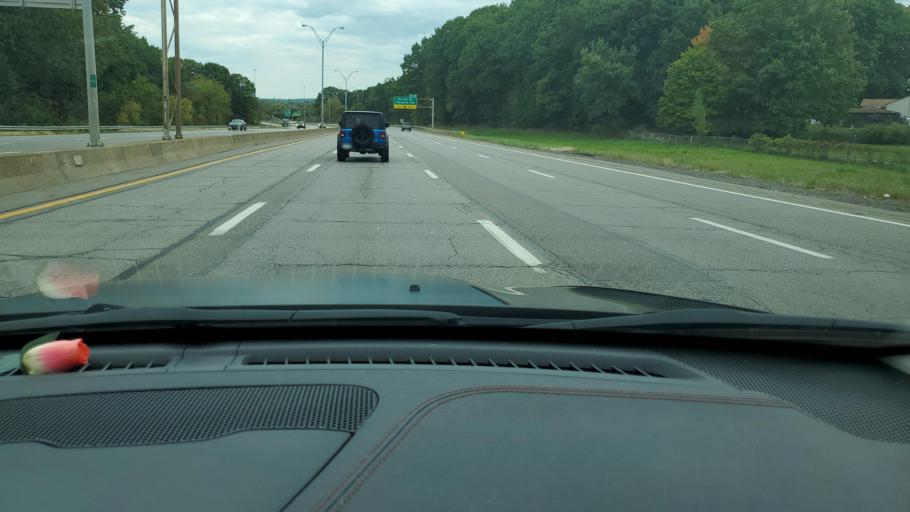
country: US
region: Ohio
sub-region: Mahoning County
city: Struthers
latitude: 41.0669
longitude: -80.6261
